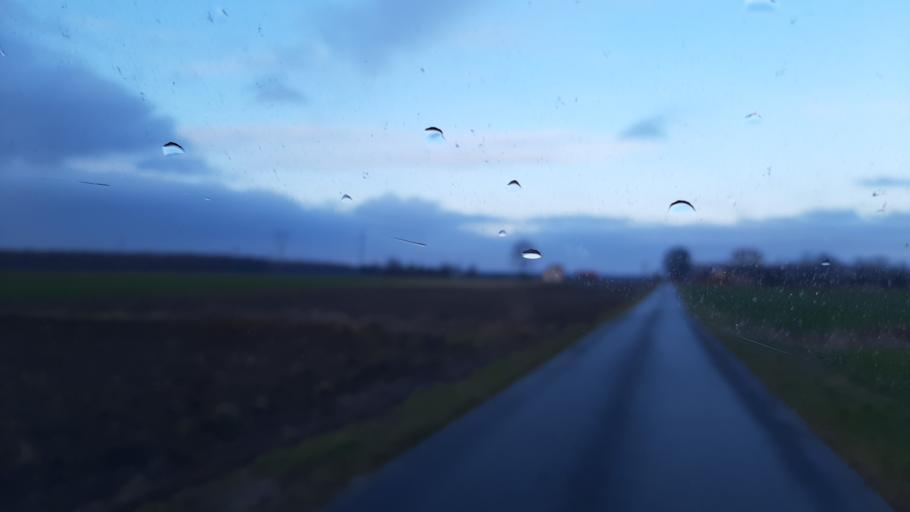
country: PL
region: Lublin Voivodeship
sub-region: Powiat lubelski
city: Garbow
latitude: 51.3622
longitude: 22.3969
